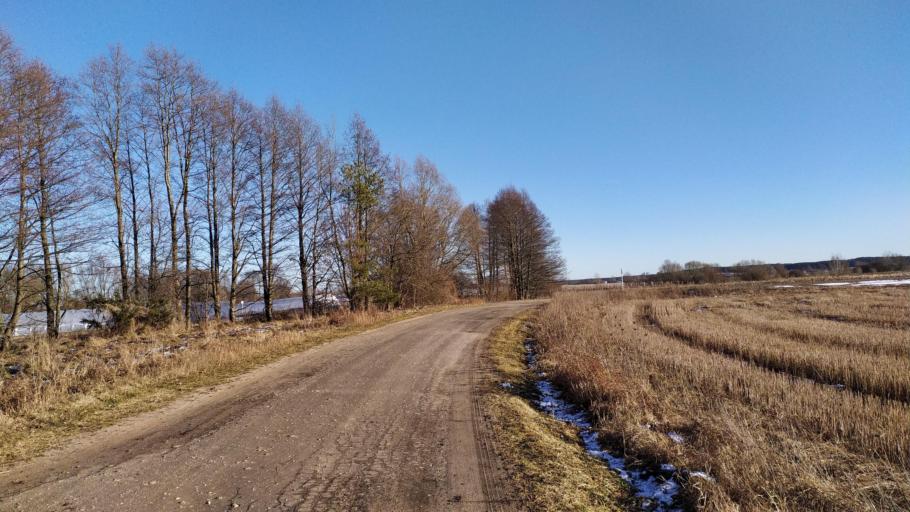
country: BY
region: Brest
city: Kamyanyets
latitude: 52.3722
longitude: 23.8923
